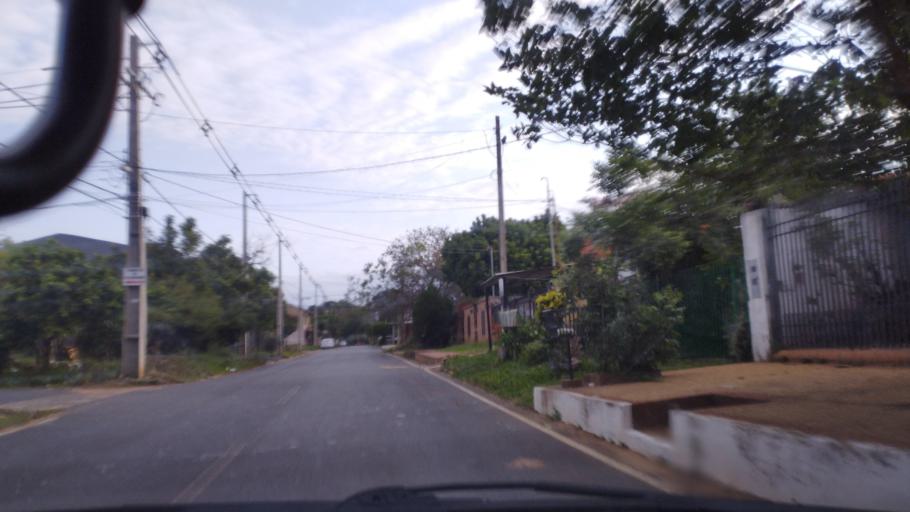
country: PY
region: Central
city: Fernando de la Mora
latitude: -25.2990
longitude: -57.5148
